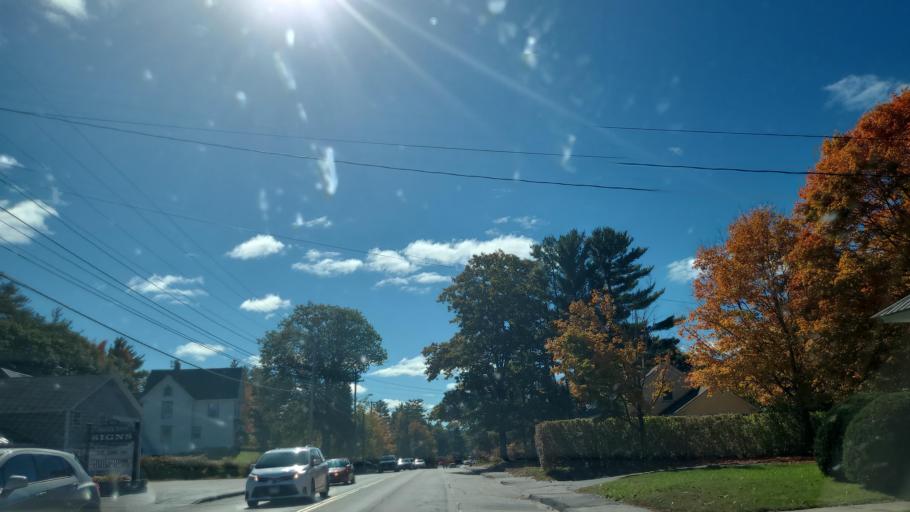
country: US
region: Maine
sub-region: Cumberland County
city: Bridgton
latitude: 44.0485
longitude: -70.7014
